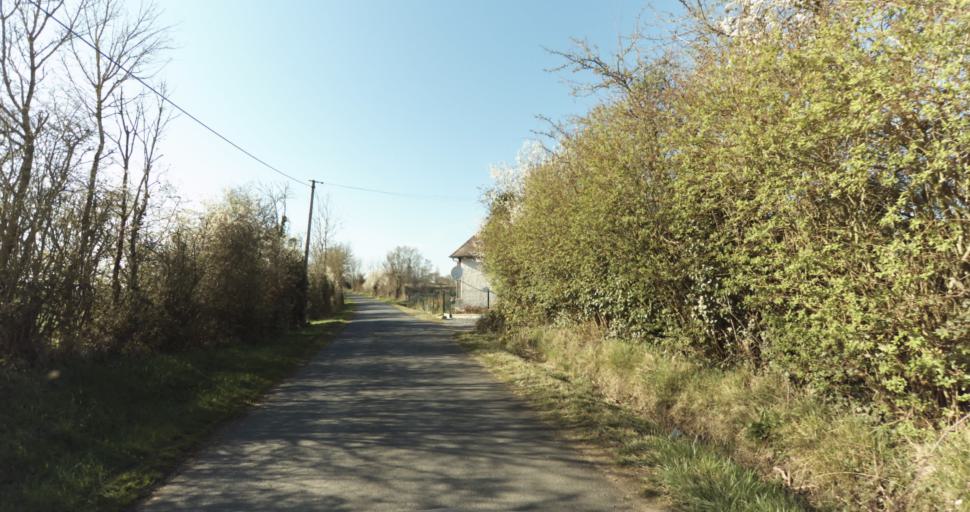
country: FR
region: Lower Normandy
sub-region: Departement du Calvados
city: Saint-Pierre-sur-Dives
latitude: 49.0430
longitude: 0.0391
